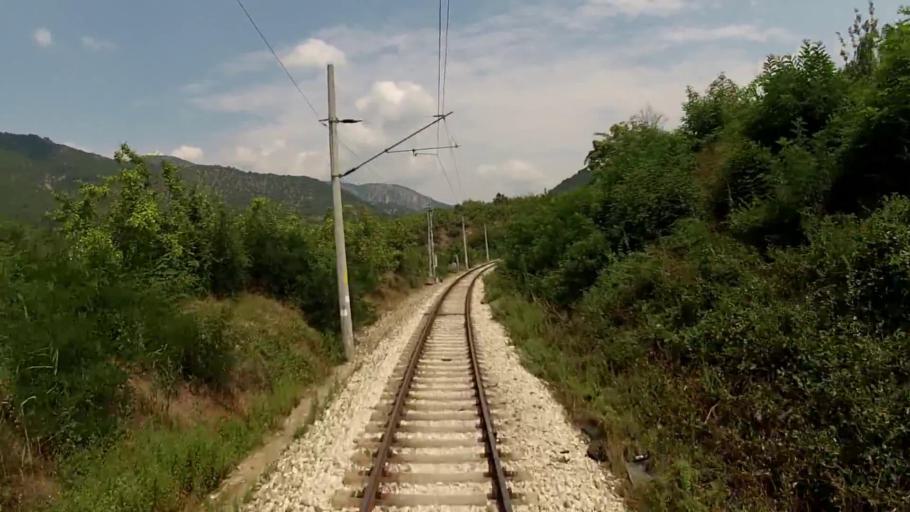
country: BG
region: Blagoevgrad
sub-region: Obshtina Kresna
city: Kresna
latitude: 41.7494
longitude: 23.1550
